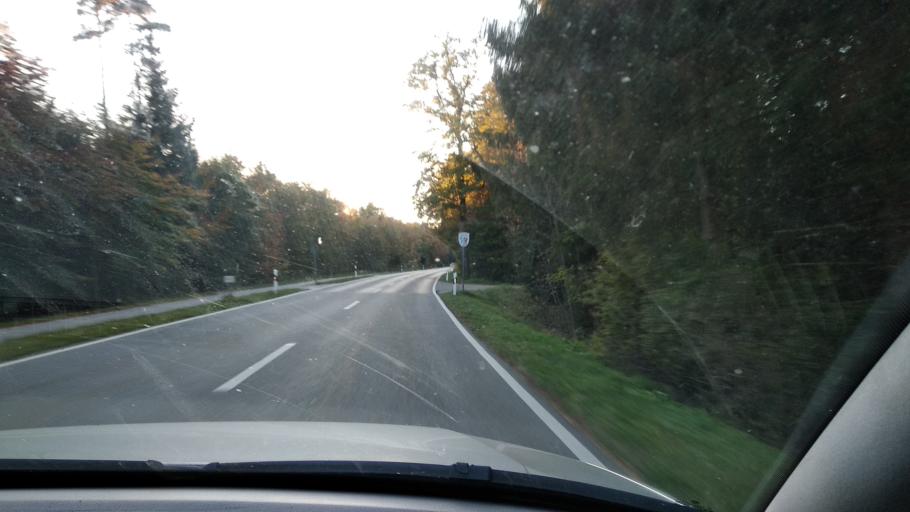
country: DE
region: Bavaria
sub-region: Upper Bavaria
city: Egmating
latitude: 48.0141
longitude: 11.7682
